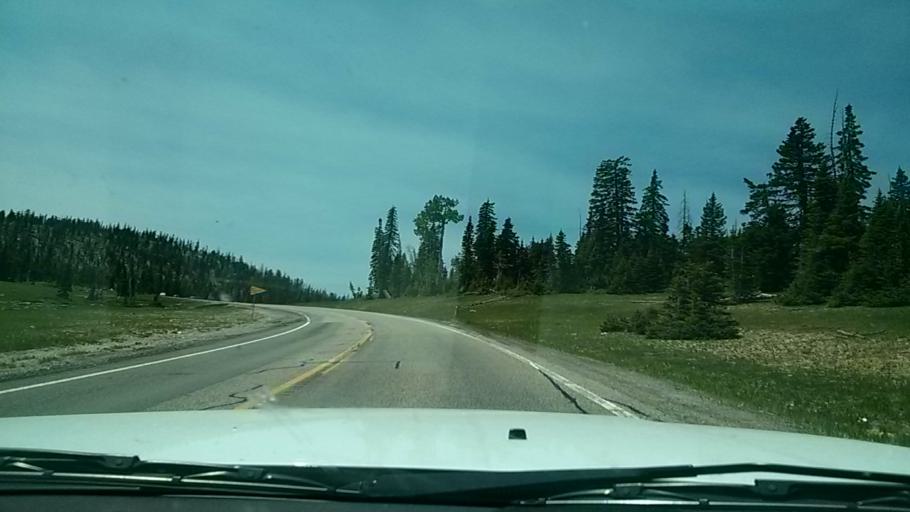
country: US
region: Utah
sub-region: Iron County
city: Cedar City
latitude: 37.5710
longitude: -112.8412
